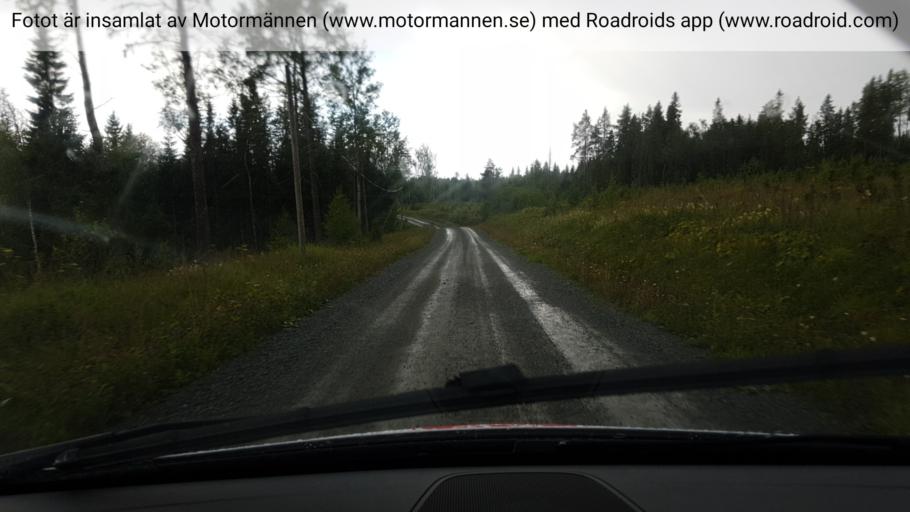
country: SE
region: Jaemtland
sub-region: OEstersunds Kommun
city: Brunflo
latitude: 63.0375
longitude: 14.7580
